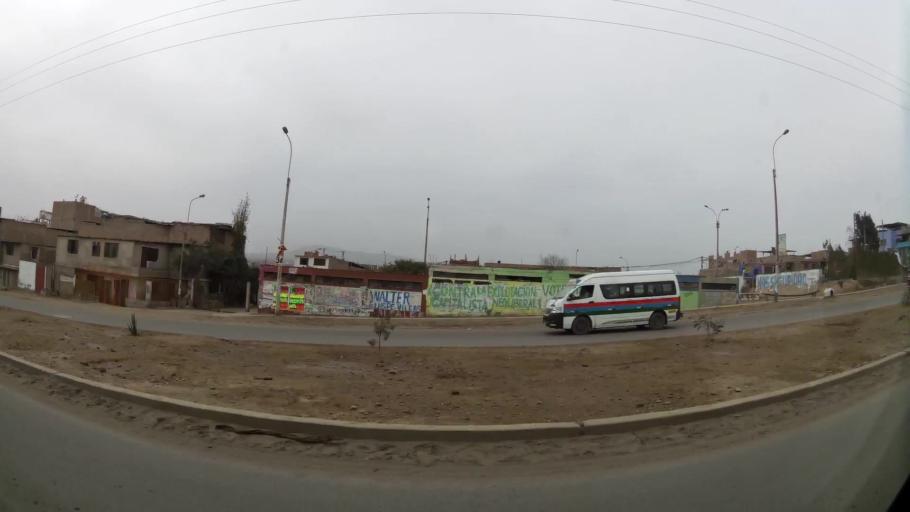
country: PE
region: Lima
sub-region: Lima
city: Surco
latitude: -12.2320
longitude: -76.9426
